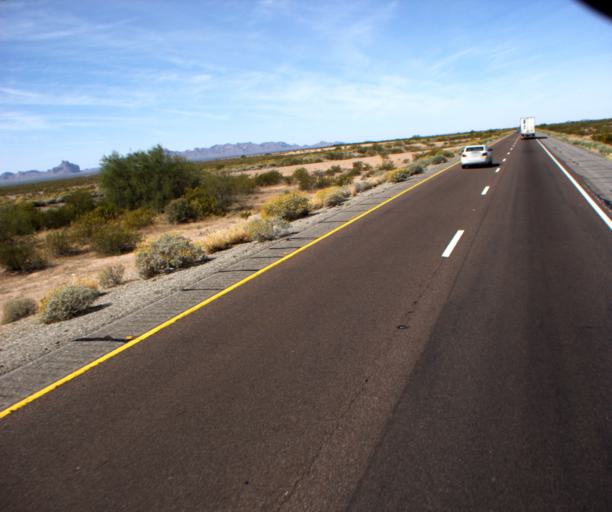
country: US
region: Arizona
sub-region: La Paz County
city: Salome
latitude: 33.5461
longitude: -113.2004
